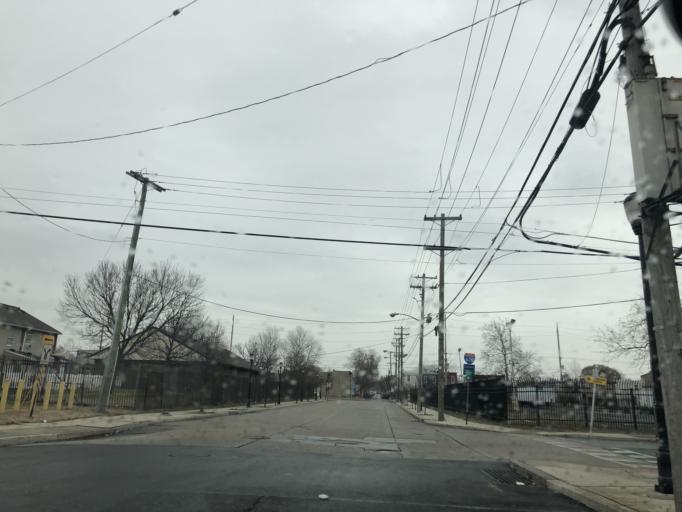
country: US
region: New Jersey
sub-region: Camden County
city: Camden
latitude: 39.9391
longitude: -75.1269
